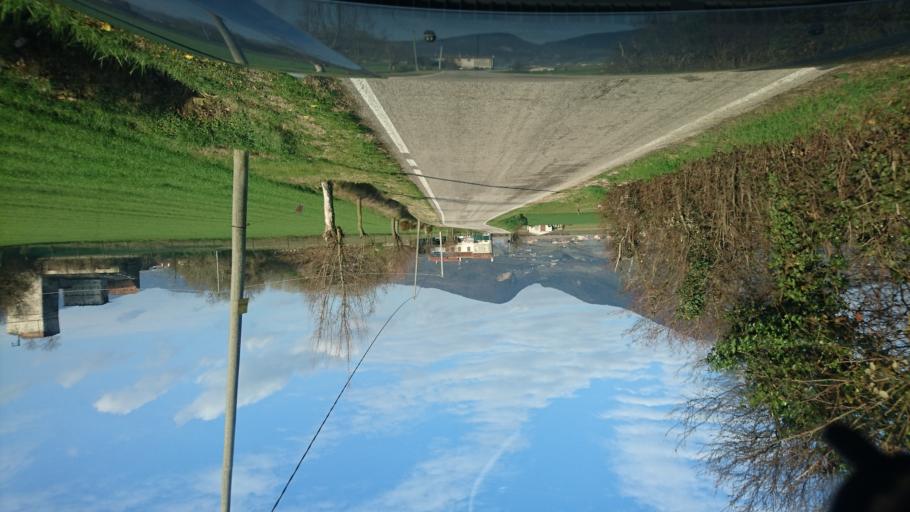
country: IT
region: Veneto
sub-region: Provincia di Padova
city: Vo
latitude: 45.3470
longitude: 11.6201
